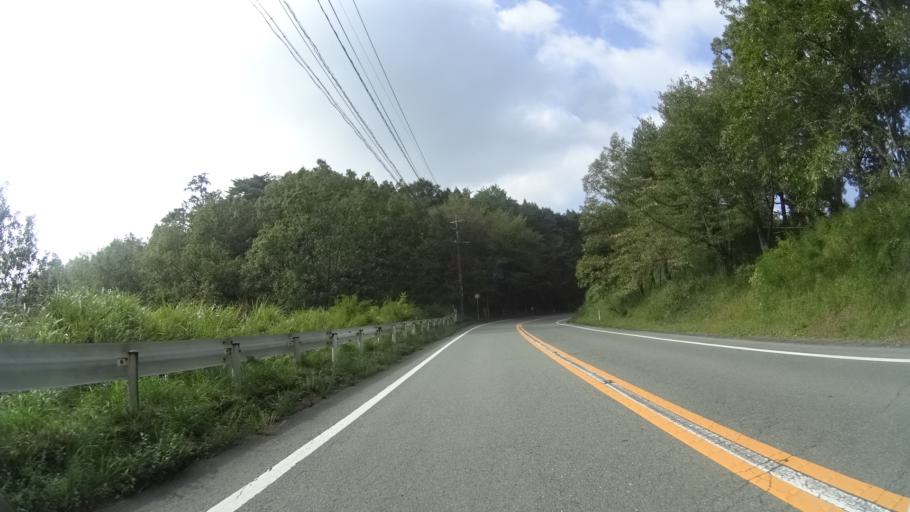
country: JP
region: Kumamoto
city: Aso
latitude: 33.0589
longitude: 131.0666
